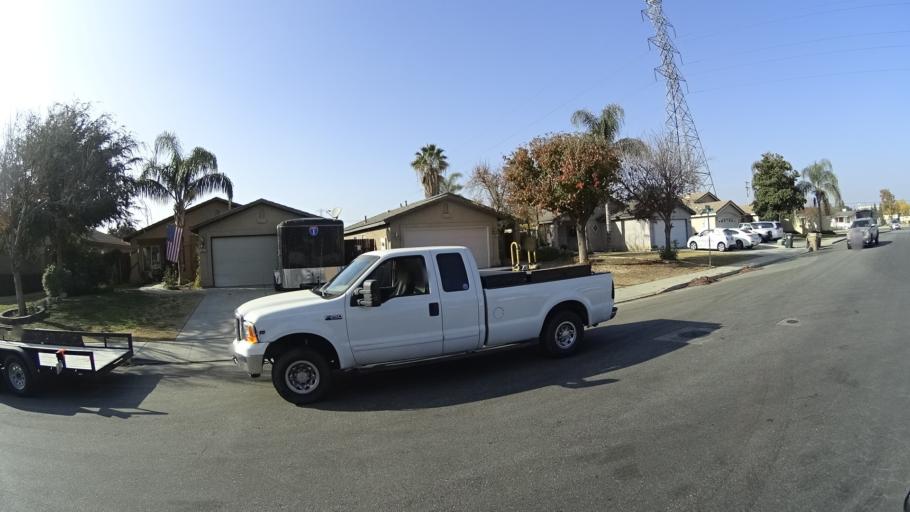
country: US
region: California
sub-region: Kern County
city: Greenacres
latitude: 35.3969
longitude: -119.0727
